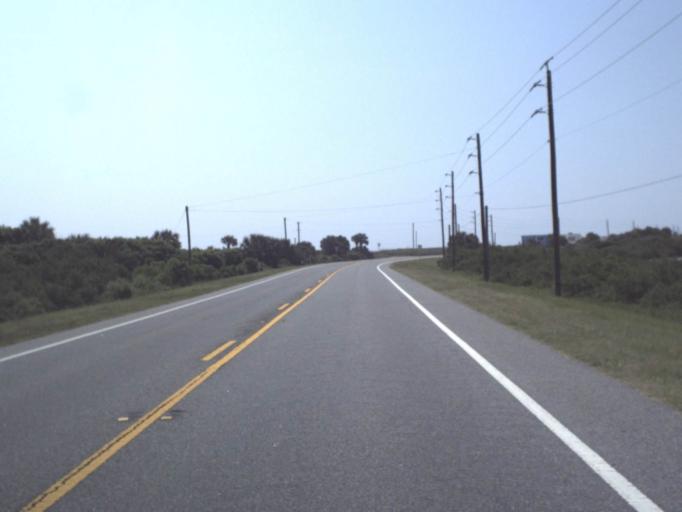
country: US
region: Florida
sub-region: Flagler County
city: Palm Coast
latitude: 29.6757
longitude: -81.2169
